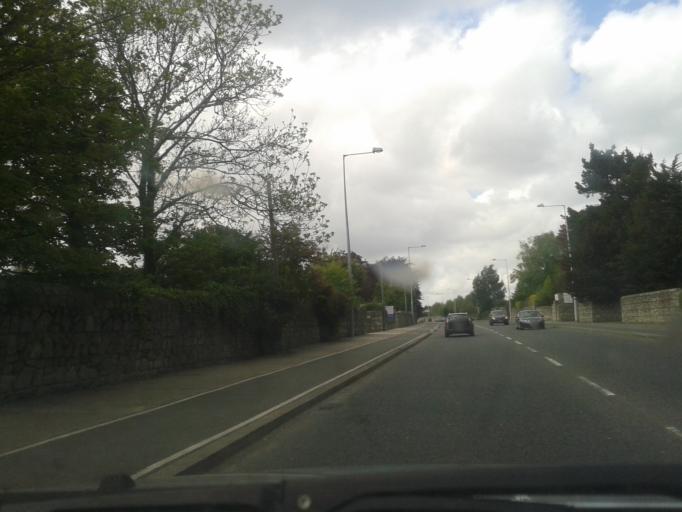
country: IE
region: Leinster
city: Loughlinstown
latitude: 53.2619
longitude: -6.1305
